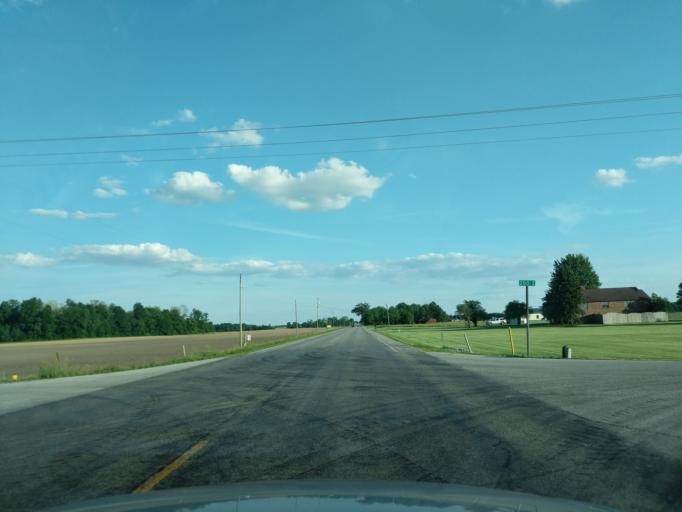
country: US
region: Indiana
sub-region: Huntington County
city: Huntington
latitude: 40.8001
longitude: -85.4607
